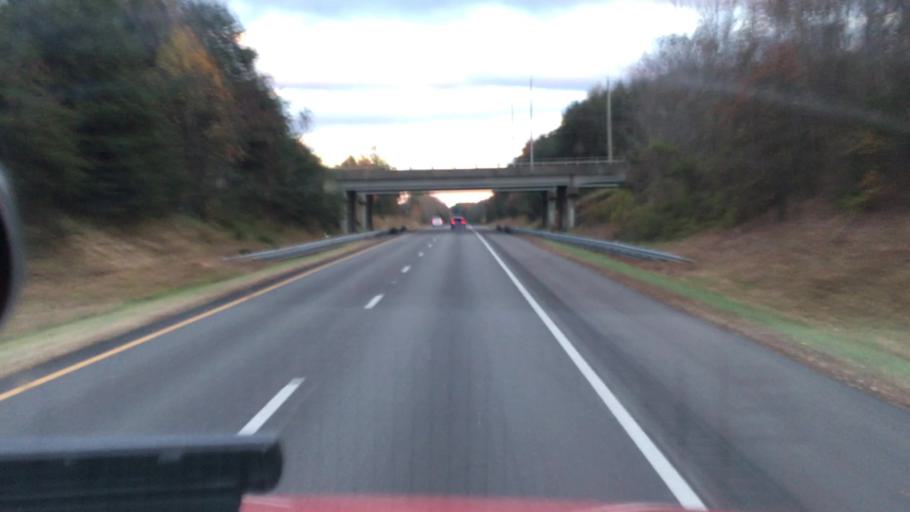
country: US
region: Virginia
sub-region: Fluvanna County
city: Palmyra
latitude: 37.9774
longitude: -78.2150
